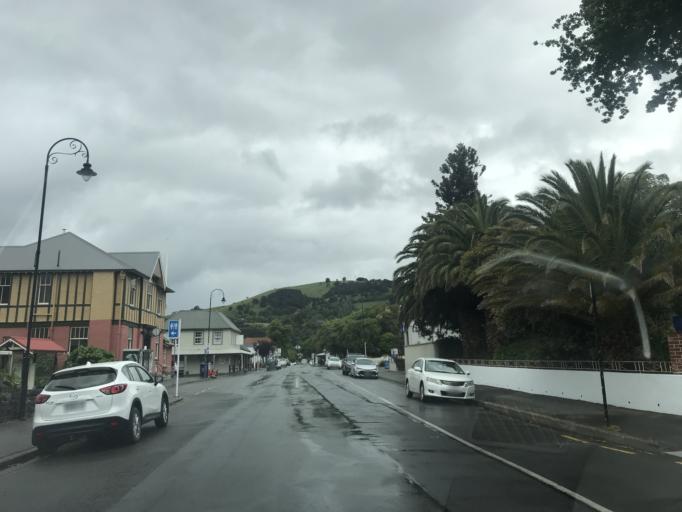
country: NZ
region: Canterbury
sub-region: Christchurch City
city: Christchurch
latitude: -43.8058
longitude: 172.9667
